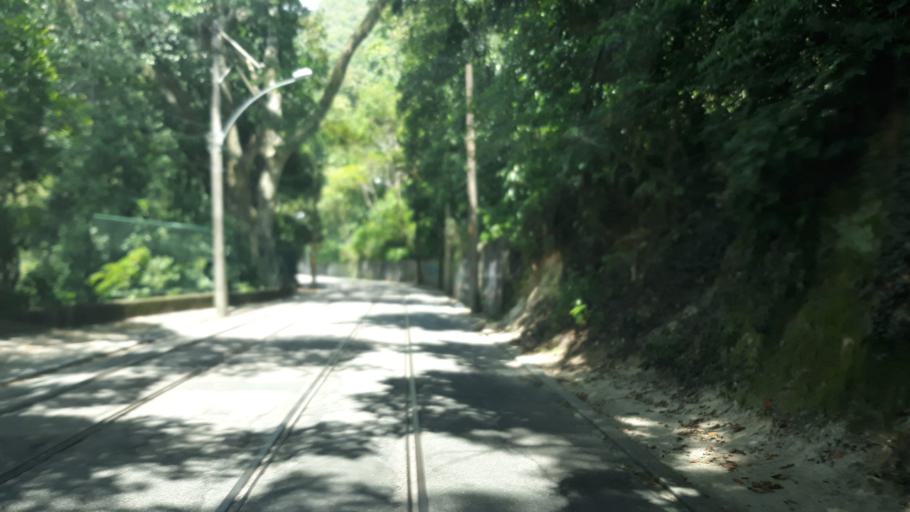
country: BR
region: Rio de Janeiro
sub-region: Rio De Janeiro
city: Rio de Janeiro
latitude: -22.9386
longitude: -43.2076
